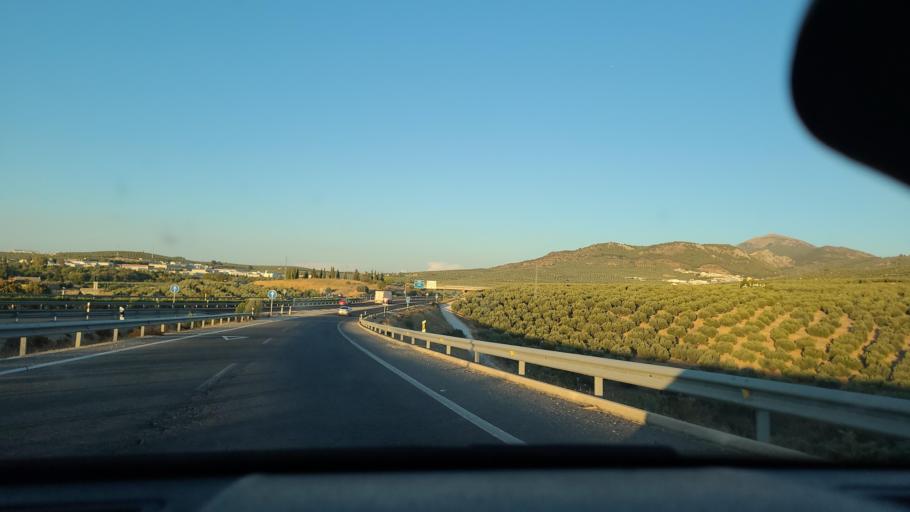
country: ES
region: Andalusia
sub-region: Provincia de Jaen
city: Torredonjimeno
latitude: 37.7522
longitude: -3.9515
